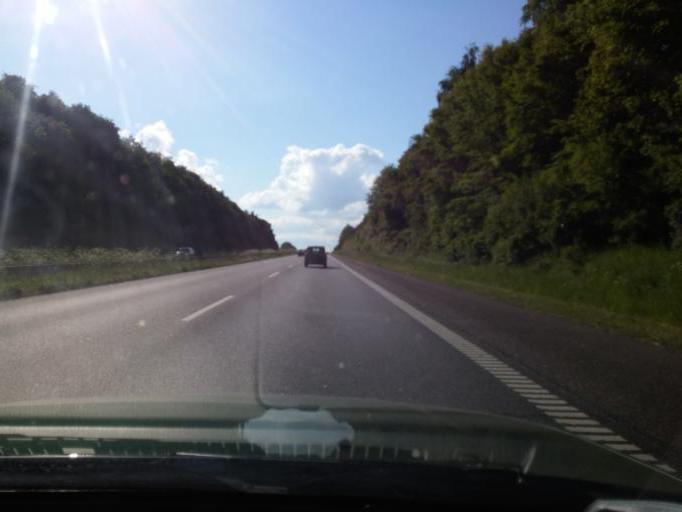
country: DK
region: South Denmark
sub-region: Fredericia Kommune
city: Taulov
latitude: 55.5435
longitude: 9.5889
